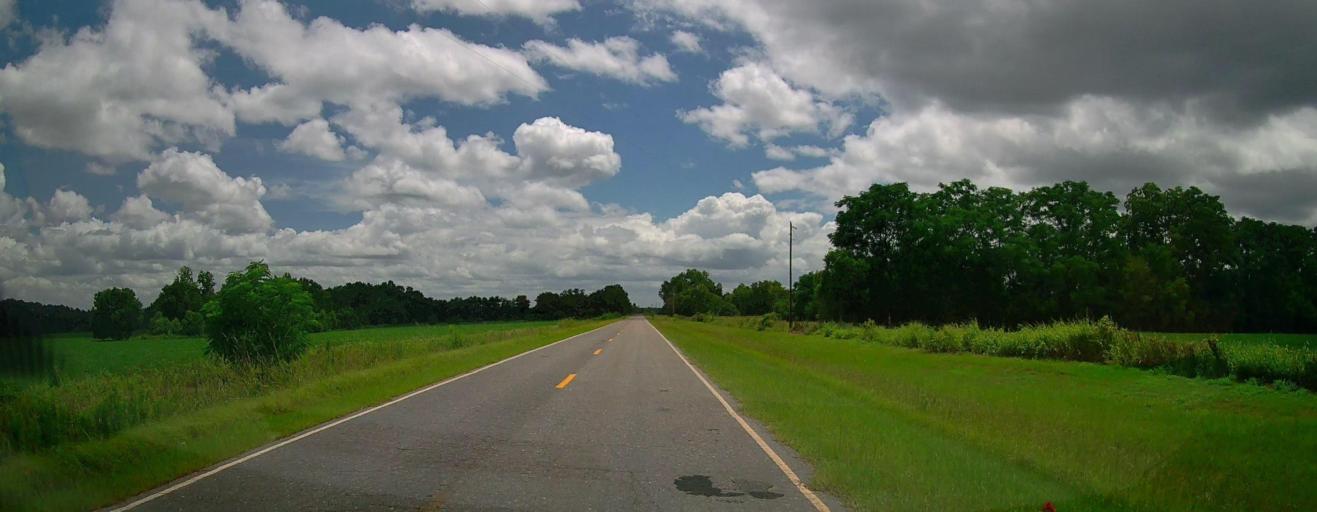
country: US
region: Georgia
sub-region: Ben Hill County
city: Fitzgerald
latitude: 31.6610
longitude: -83.4009
